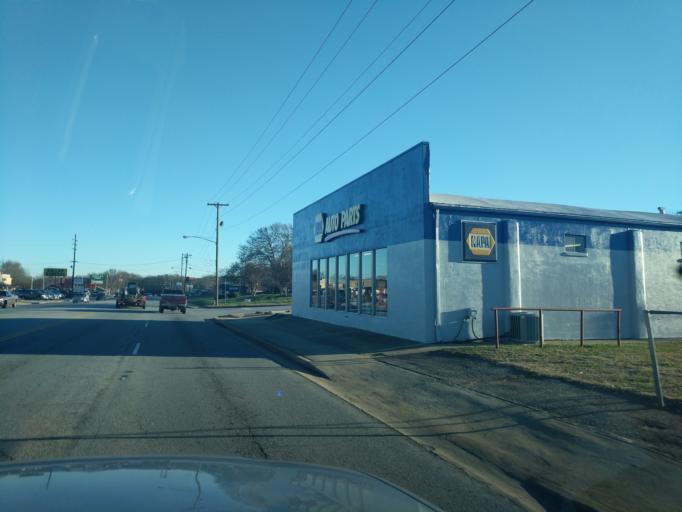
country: US
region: South Carolina
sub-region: Oconee County
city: Westminster
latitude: 34.6621
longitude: -83.0922
